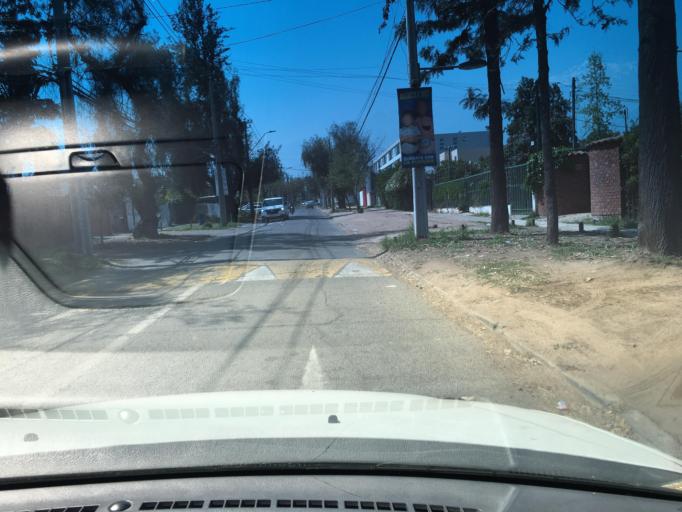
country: CL
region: Santiago Metropolitan
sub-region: Provincia de Santiago
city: Villa Presidente Frei, Nunoa, Santiago, Chile
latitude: -33.5201
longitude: -70.5664
